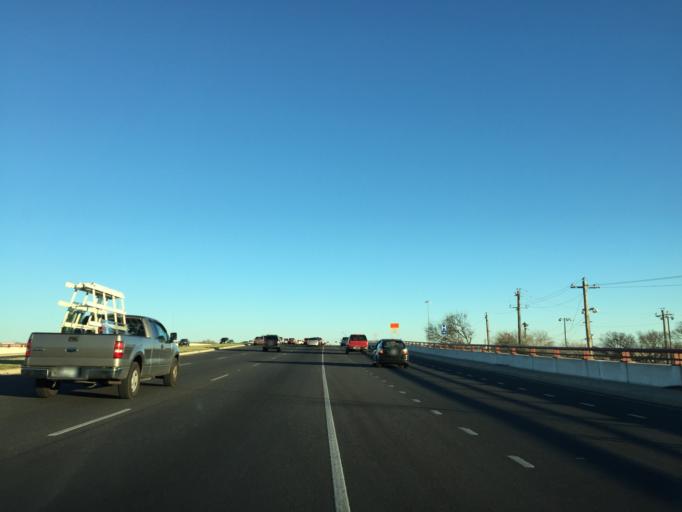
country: US
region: Texas
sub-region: Travis County
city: Wells Branch
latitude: 30.4220
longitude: -97.7077
